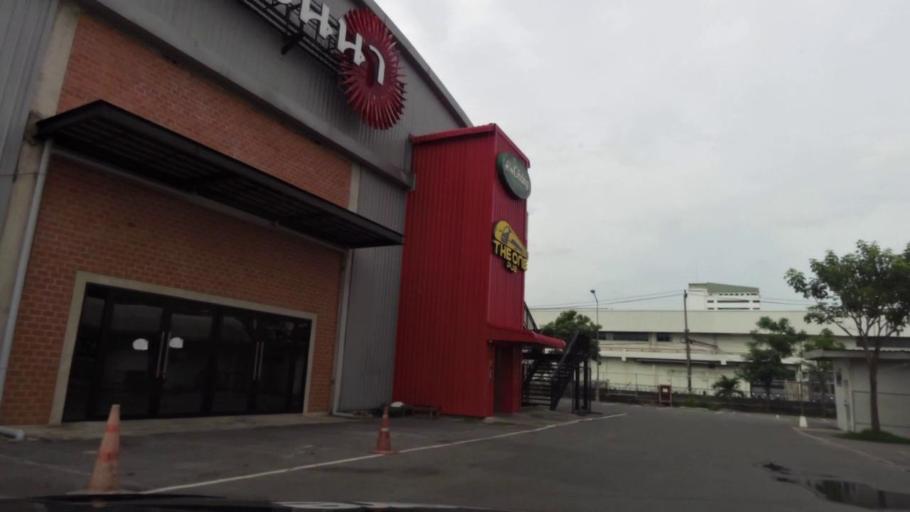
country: TH
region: Bangkok
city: Bang Kapi
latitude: 13.7650
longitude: 100.6395
